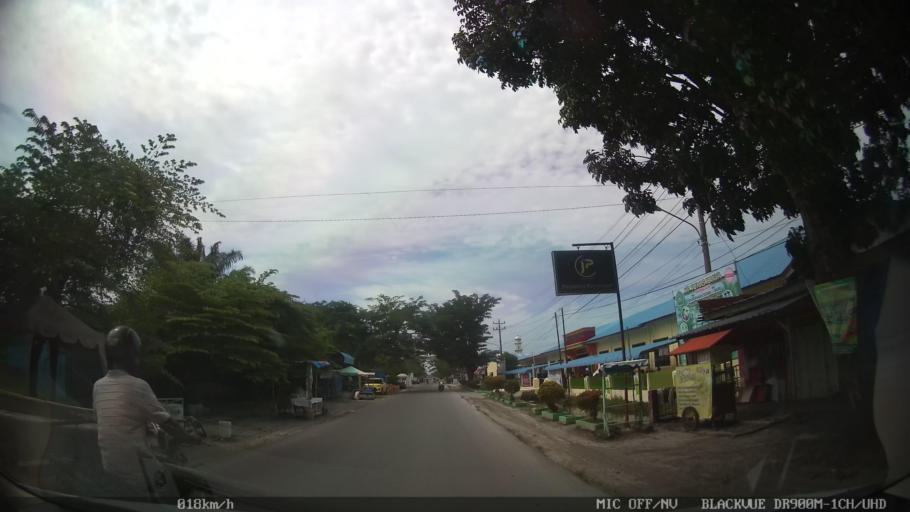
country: ID
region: North Sumatra
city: Percut
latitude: 3.6106
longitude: 98.8077
